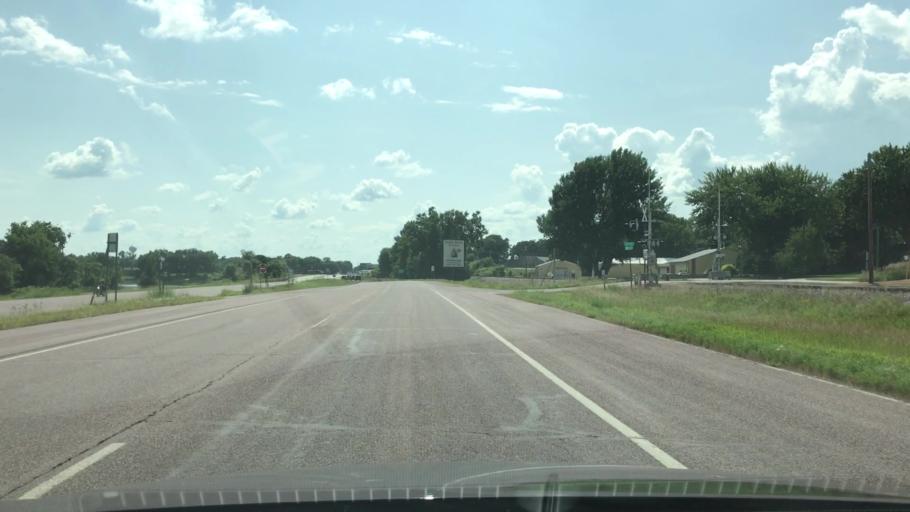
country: US
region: Minnesota
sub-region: Blue Earth County
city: Lake Crystal
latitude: 44.1172
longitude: -94.2078
